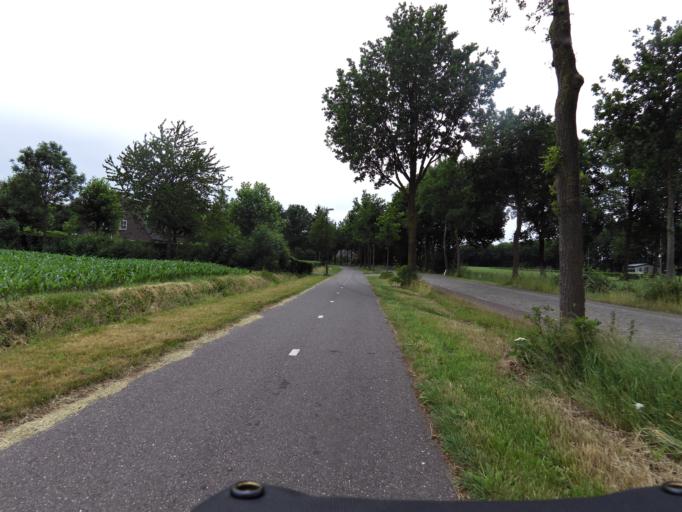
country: NL
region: North Brabant
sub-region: Gemeente Bladel en Netersel
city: Bladel
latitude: 51.3995
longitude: 5.2060
